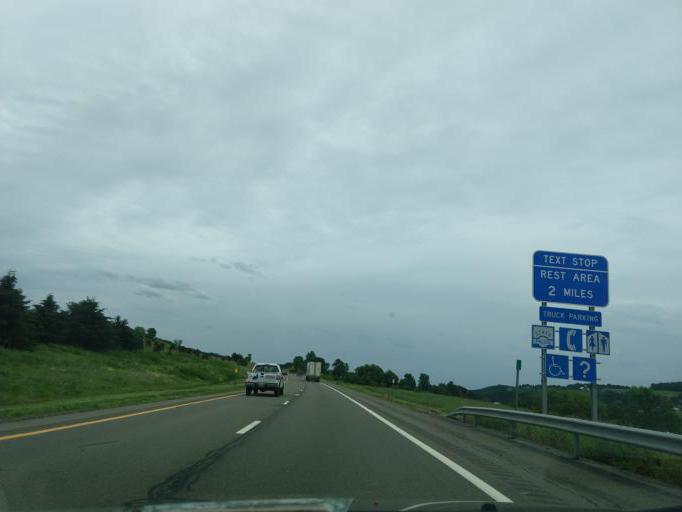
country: US
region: New York
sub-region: Chenango County
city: Lakeview
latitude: 42.4049
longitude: -76.0135
